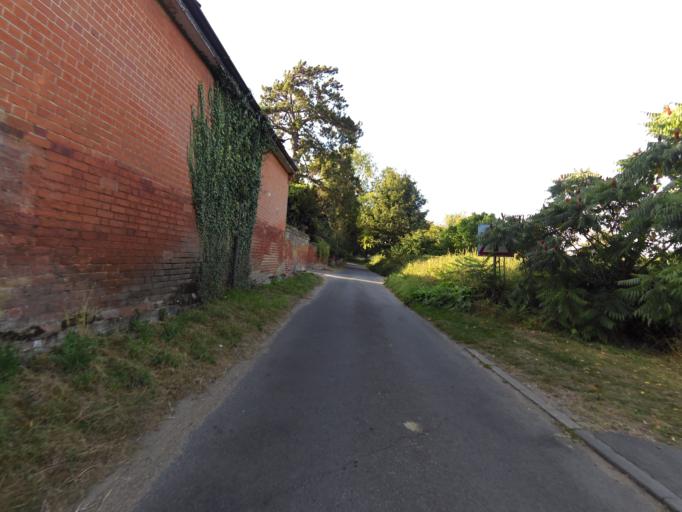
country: GB
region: England
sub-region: Suffolk
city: Kesgrave
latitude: 52.0100
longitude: 1.2312
